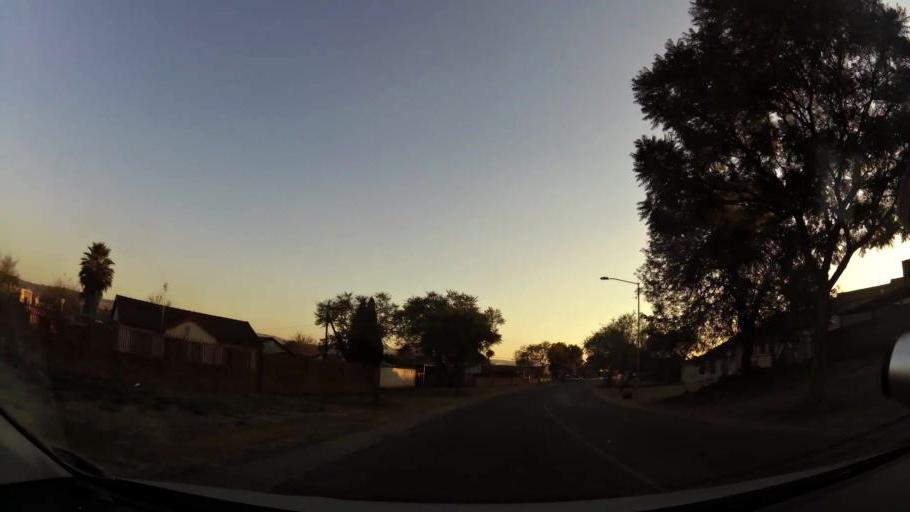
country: ZA
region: Gauteng
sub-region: City of Tshwane Metropolitan Municipality
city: Pretoria
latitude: -25.7410
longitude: 28.1406
